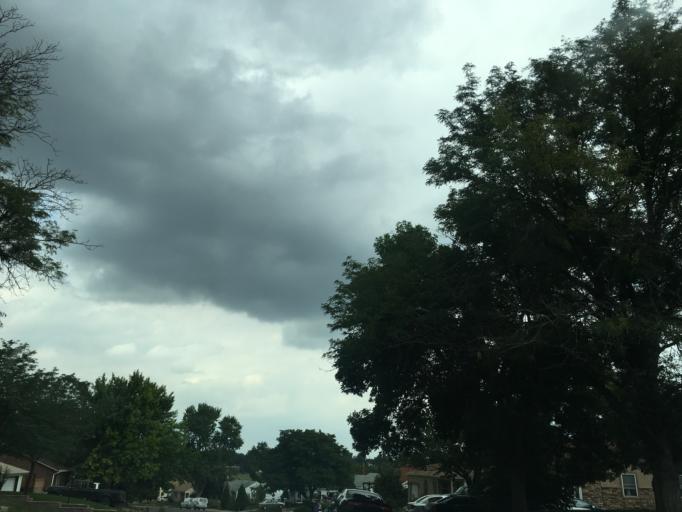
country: US
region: Colorado
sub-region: Arapahoe County
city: Sheridan
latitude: 39.6856
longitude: -105.0119
